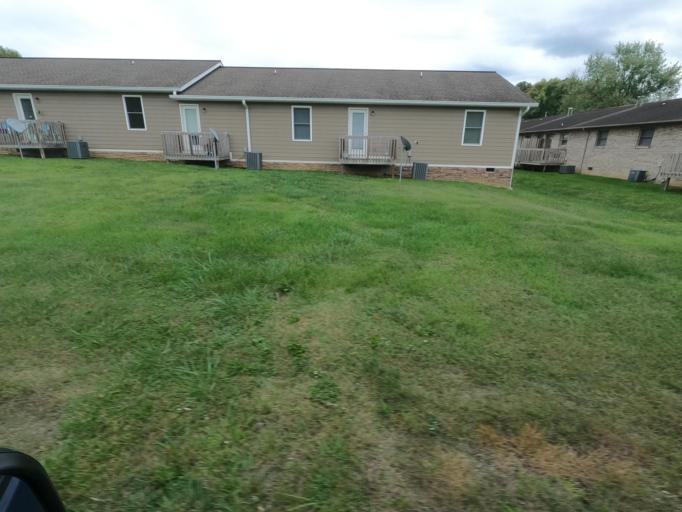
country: US
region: Tennessee
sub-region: Carter County
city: Central
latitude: 36.3357
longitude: -82.2607
